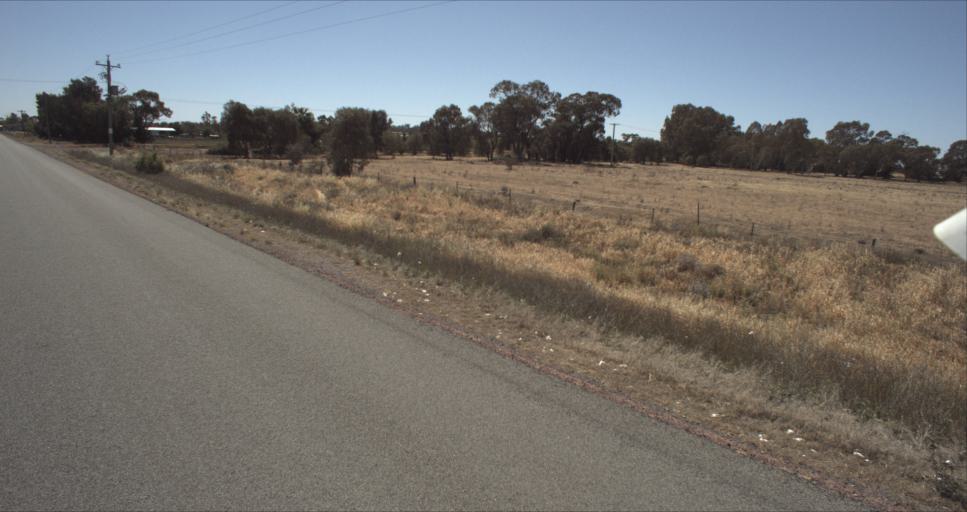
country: AU
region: New South Wales
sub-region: Leeton
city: Leeton
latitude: -34.4322
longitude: 146.2994
